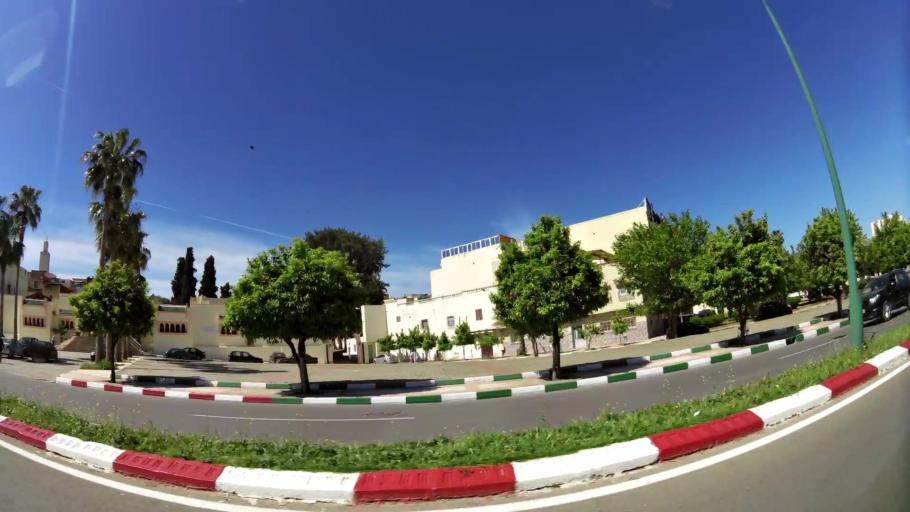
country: MA
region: Meknes-Tafilalet
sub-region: Meknes
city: Meknes
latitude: 33.8927
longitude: -5.5548
